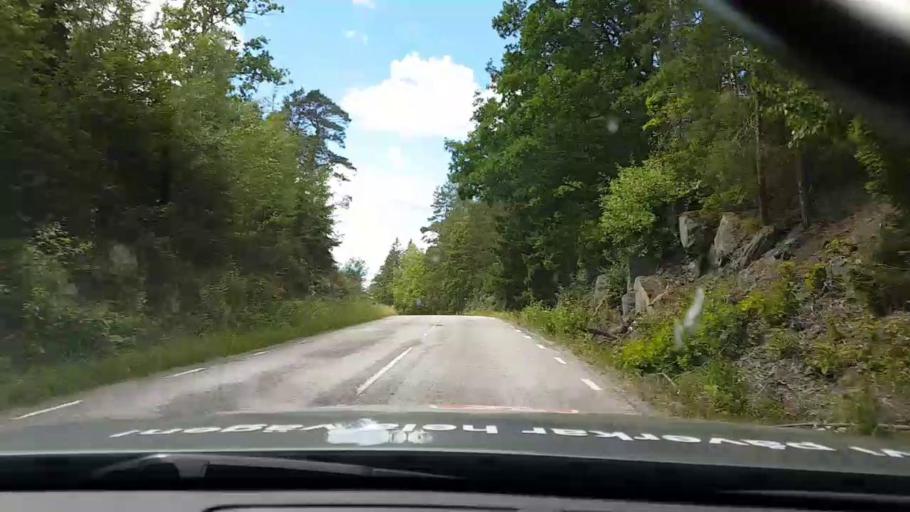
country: SE
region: Kalmar
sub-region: Vasterviks Kommun
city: Forserum
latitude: 58.0204
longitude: 16.5261
